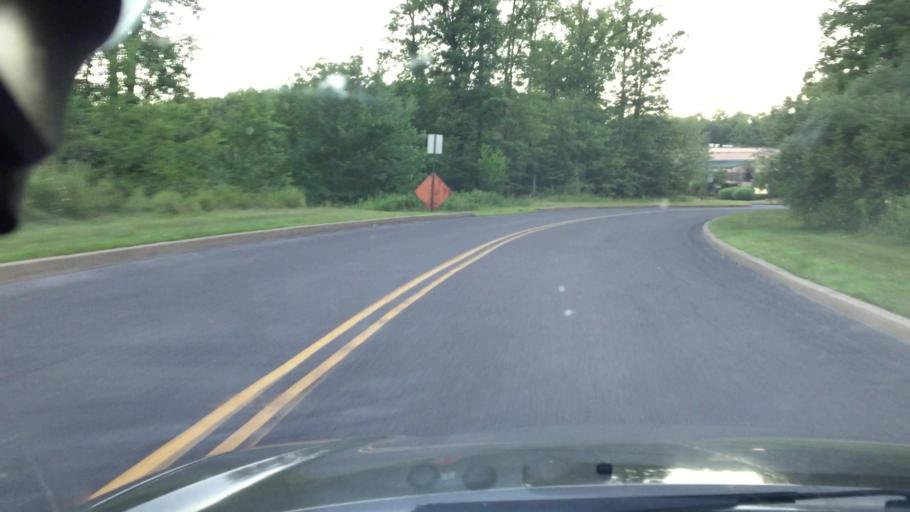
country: US
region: Pennsylvania
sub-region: Luzerne County
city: Harleigh
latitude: 41.0443
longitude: -75.9652
